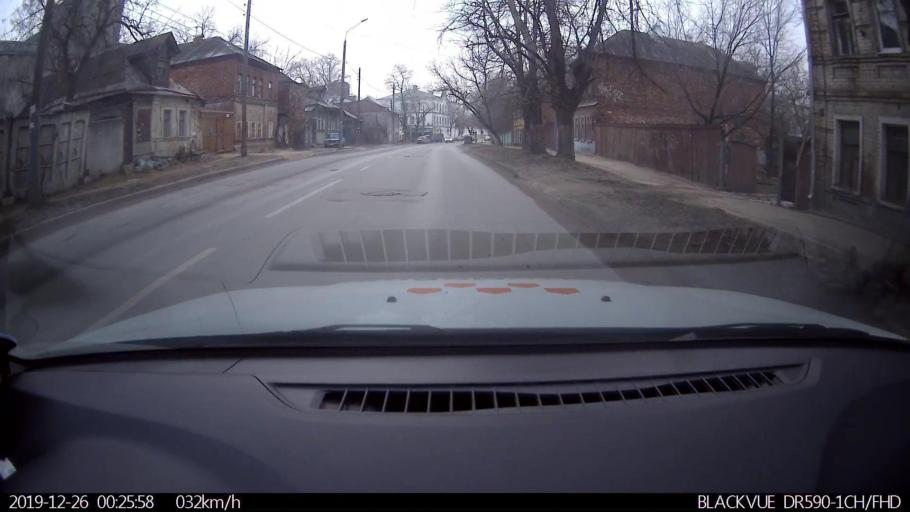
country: RU
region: Nizjnij Novgorod
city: Nizhniy Novgorod
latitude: 56.3157
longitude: 43.9521
